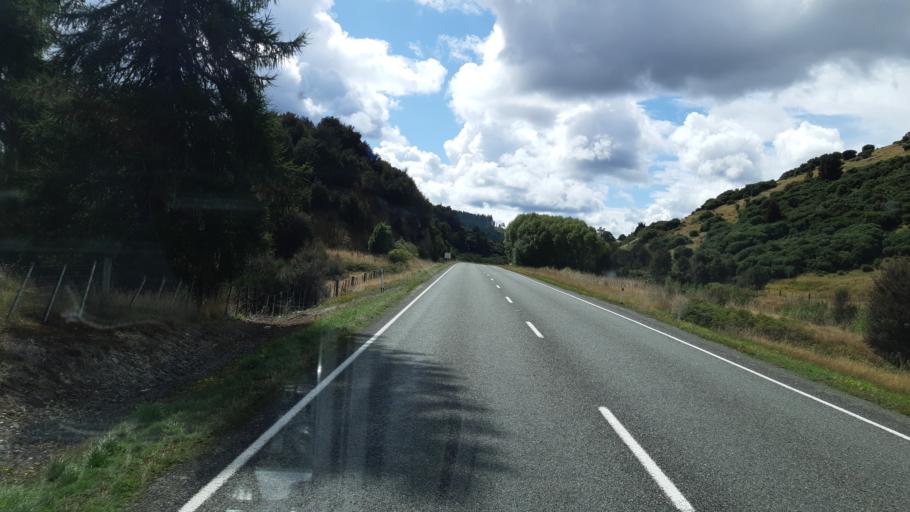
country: NZ
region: Tasman
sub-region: Tasman District
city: Wakefield
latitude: -41.6472
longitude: 172.6535
